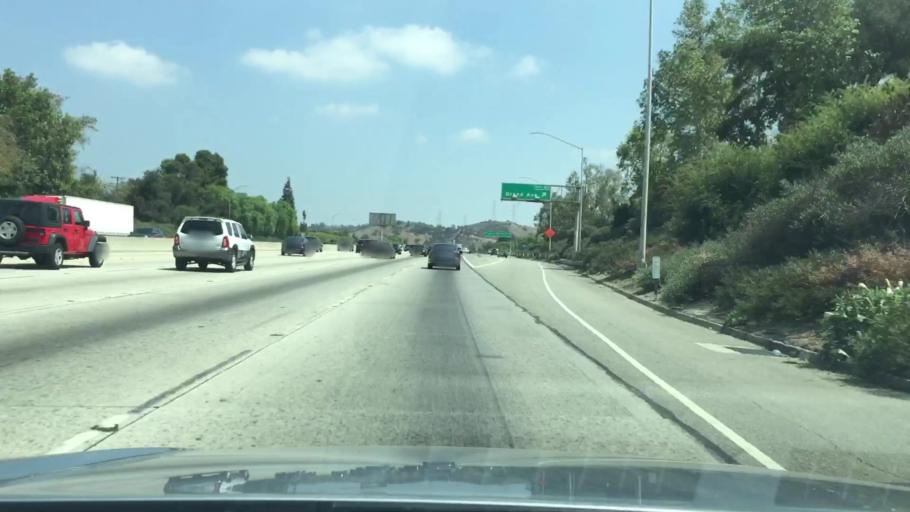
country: US
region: California
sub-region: Los Angeles County
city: Citrus
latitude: 34.1208
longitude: -117.8796
